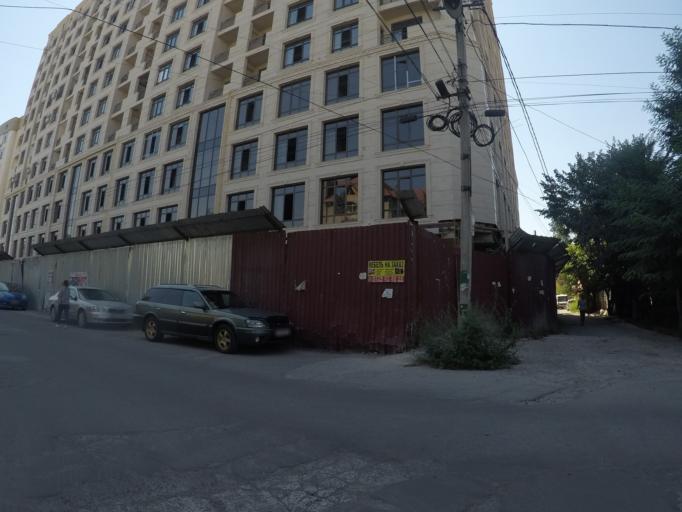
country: KG
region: Chuy
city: Bishkek
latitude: 42.8802
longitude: 74.5936
